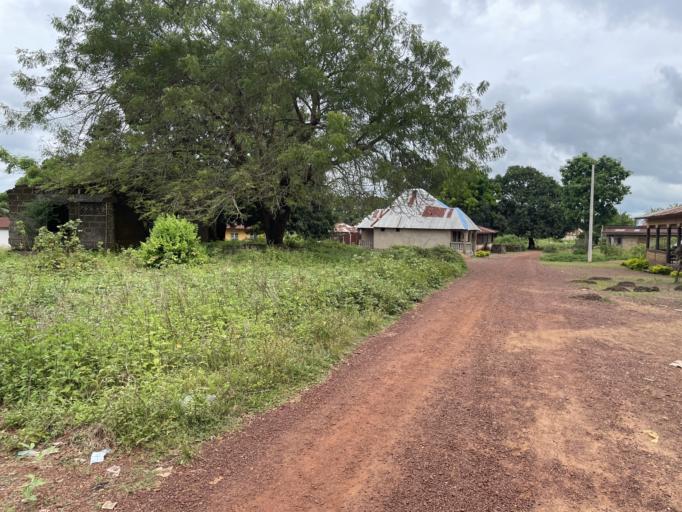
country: SL
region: Northern Province
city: Kambia
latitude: 9.1292
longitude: -12.9084
